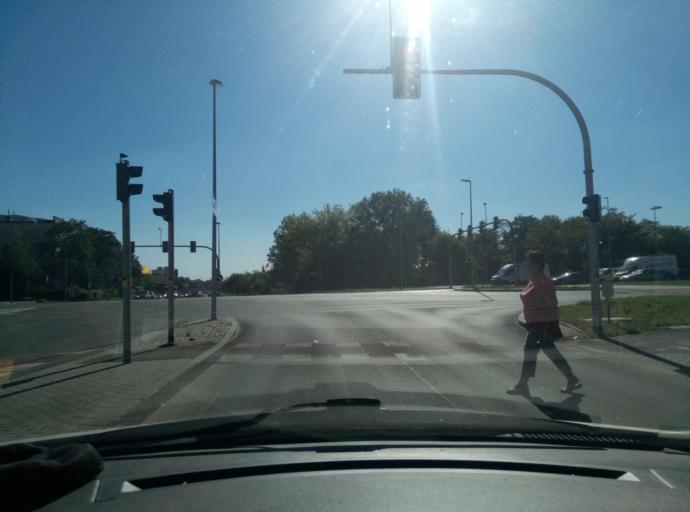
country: PL
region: Kujawsko-Pomorskie
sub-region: Torun
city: Torun
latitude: 53.0215
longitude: 18.5967
